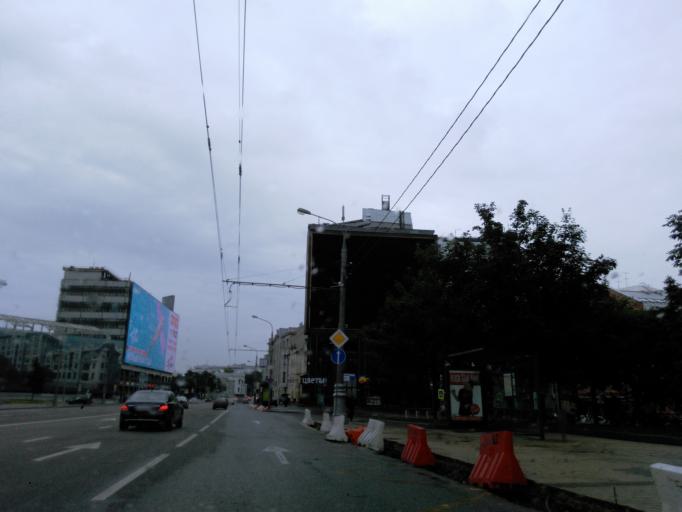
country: RU
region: Moscow
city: Moscow
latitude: 55.7527
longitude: 37.5960
